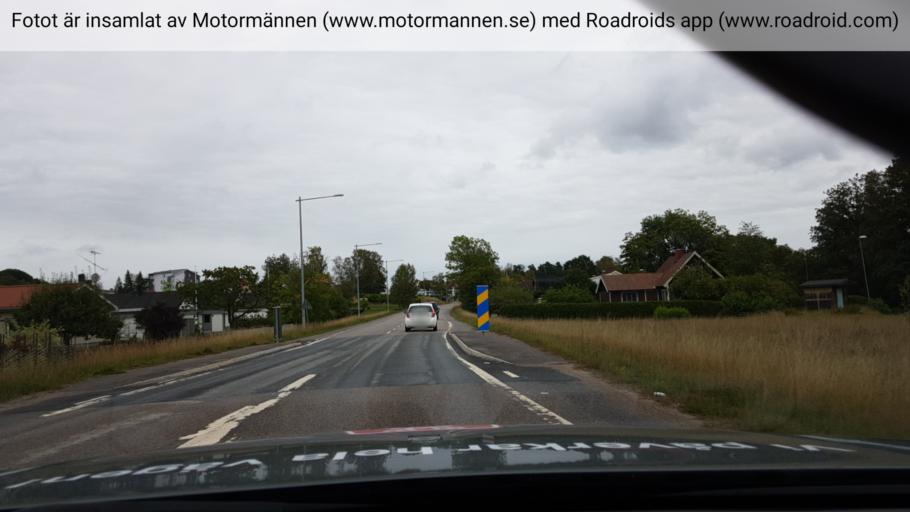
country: SE
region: Soedermanland
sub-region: Trosa Kommun
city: Vagnharad
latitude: 58.9426
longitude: 17.4818
